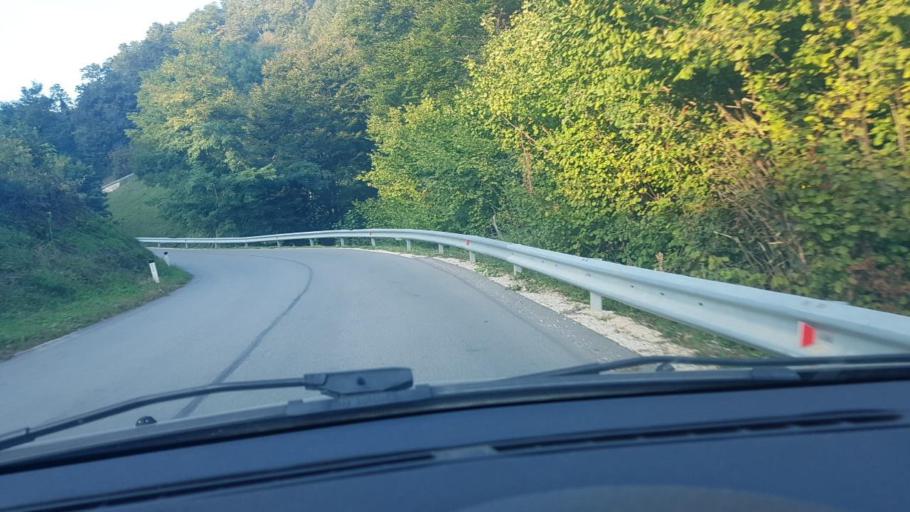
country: SI
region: Rogatec
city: Rogatec
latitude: 46.2637
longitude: 15.7059
